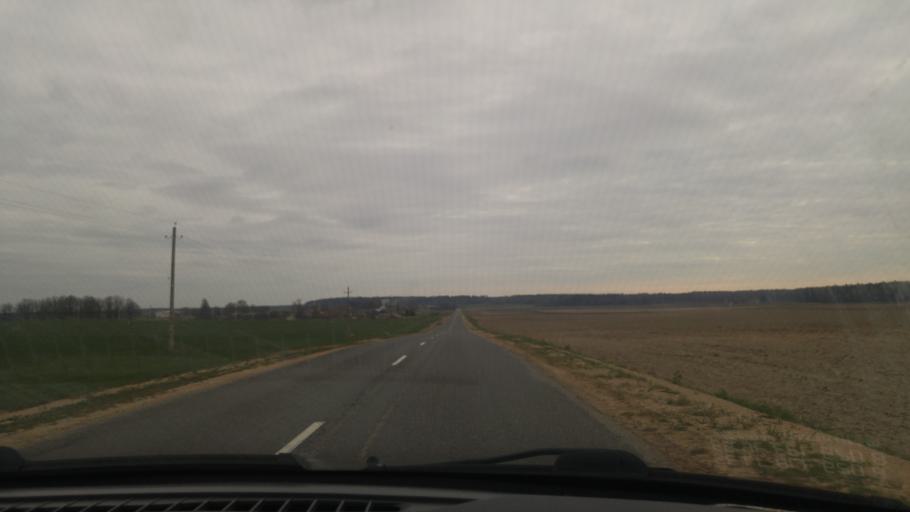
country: BY
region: Minsk
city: Chervyen'
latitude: 53.7222
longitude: 28.2619
